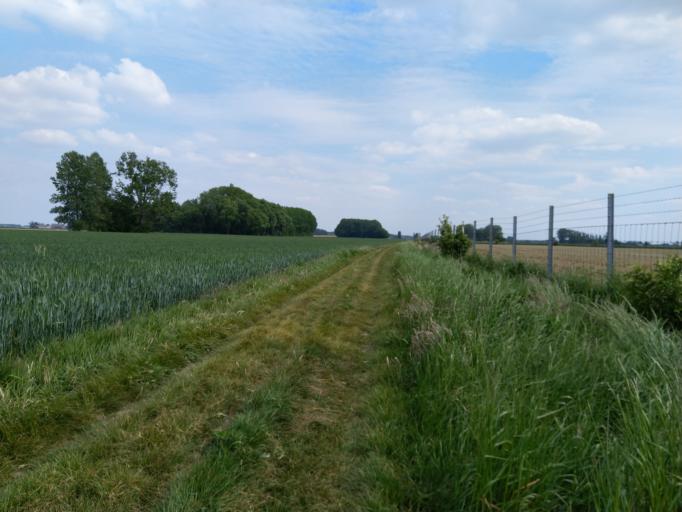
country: BE
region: Wallonia
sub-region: Province du Hainaut
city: Jurbise
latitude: 50.5467
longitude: 3.9350
